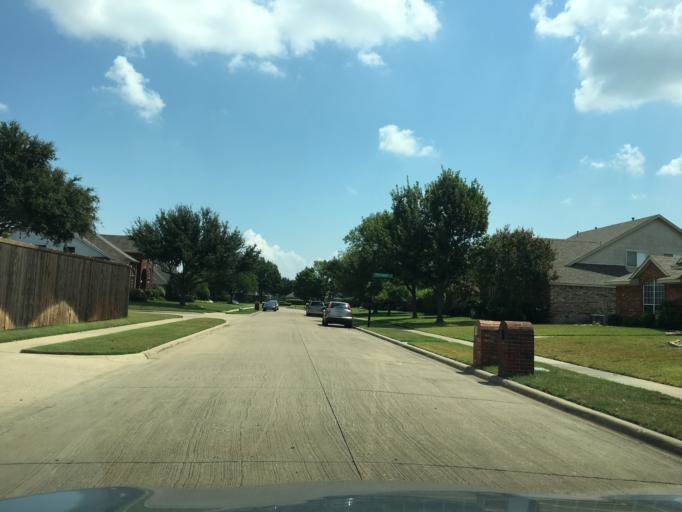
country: US
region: Texas
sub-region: Dallas County
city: Garland
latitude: 32.9409
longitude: -96.6458
